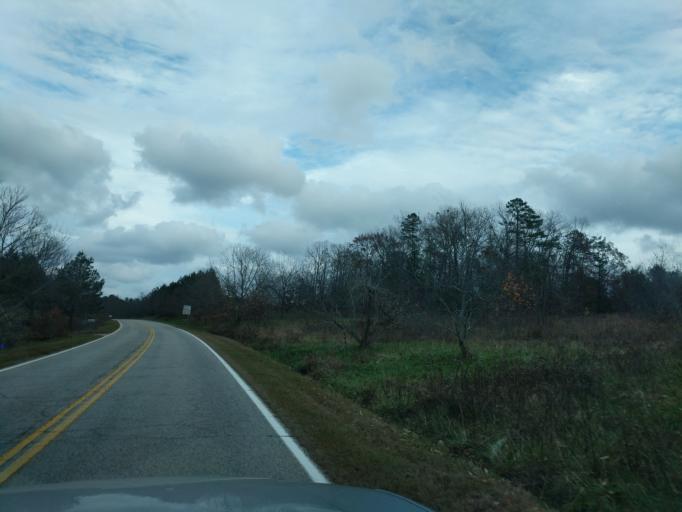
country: US
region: South Carolina
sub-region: Greenwood County
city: Ware Shoals
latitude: 34.3773
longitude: -82.1680
